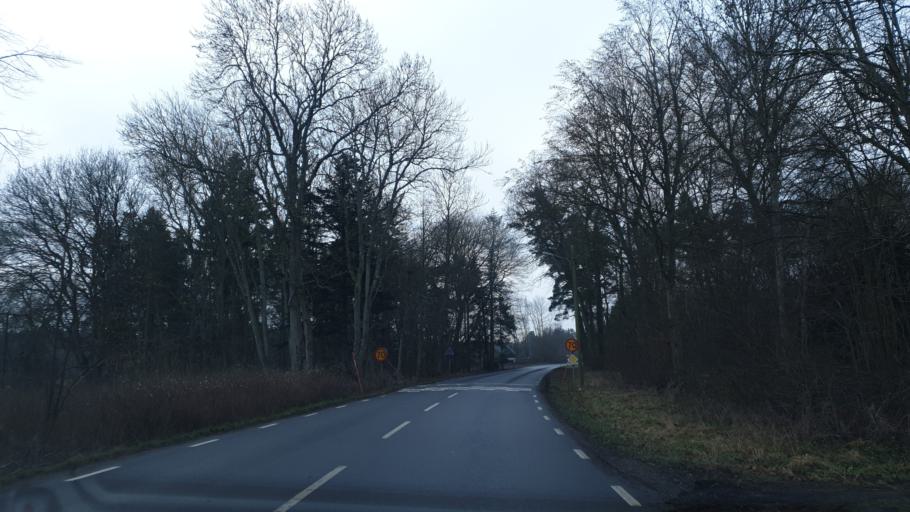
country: SE
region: Skane
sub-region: Kristianstads Kommun
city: Fjalkinge
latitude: 56.0186
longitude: 14.3729
